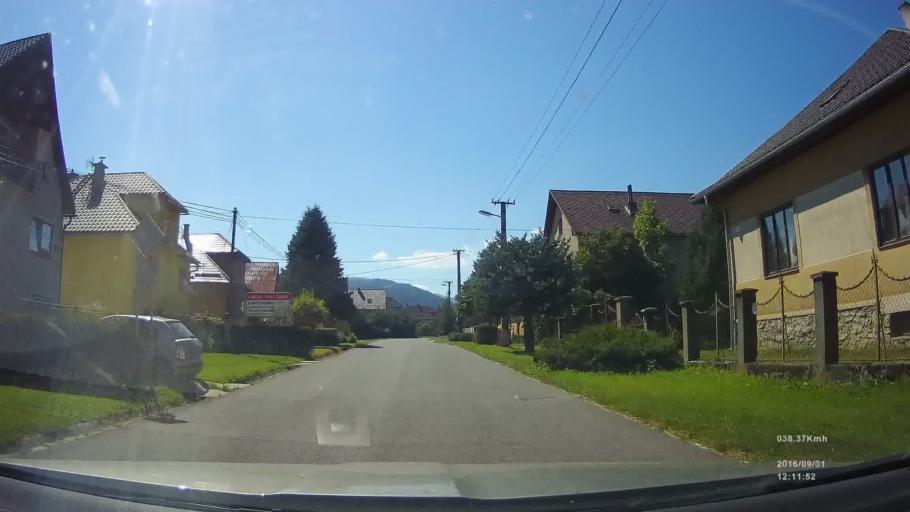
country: SK
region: Zilinsky
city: Ruzomberok
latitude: 49.0609
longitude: 19.4333
